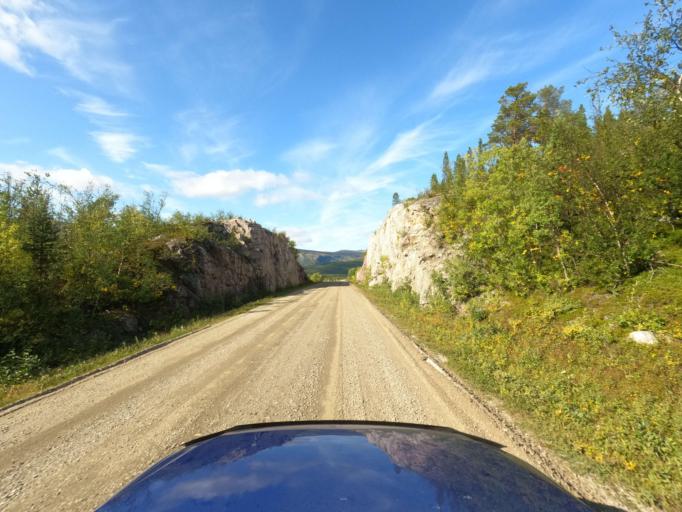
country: NO
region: Finnmark Fylke
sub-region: Porsanger
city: Lakselv
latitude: 69.8901
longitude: 25.0032
